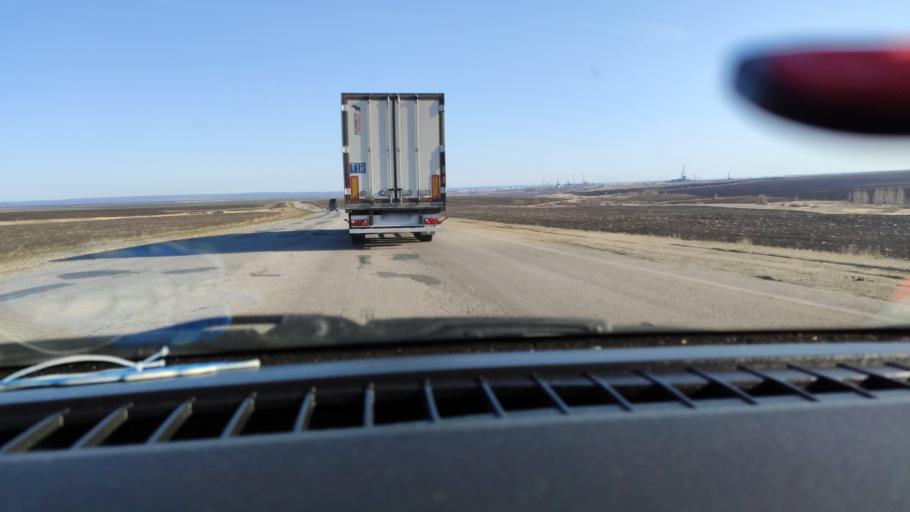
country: RU
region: Samara
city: Syzran'
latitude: 53.0057
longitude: 48.3319
